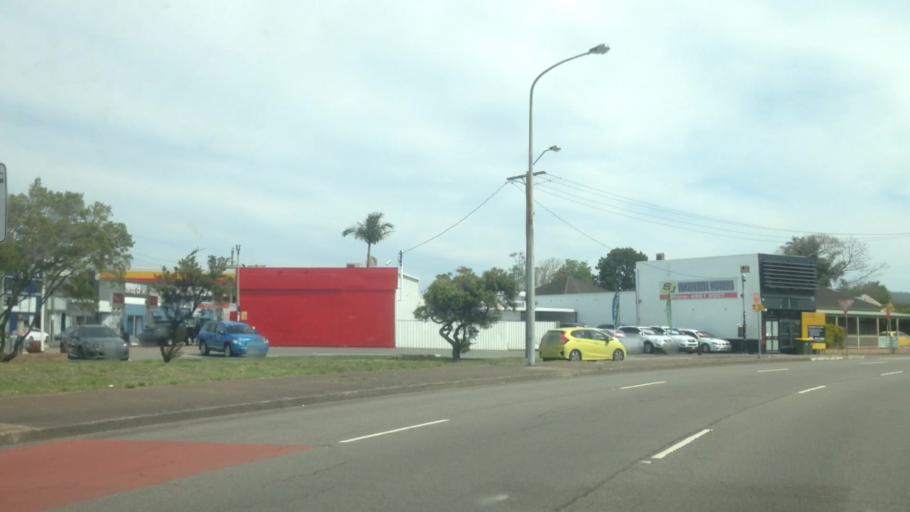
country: AU
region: New South Wales
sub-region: Newcastle
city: Broadmeadow
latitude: -32.9245
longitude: 151.7368
